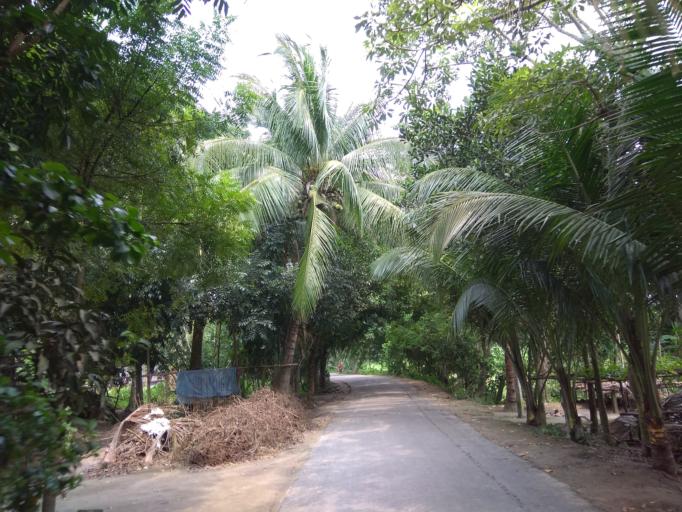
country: BD
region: Dhaka
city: Dohar
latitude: 23.4992
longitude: 90.0105
